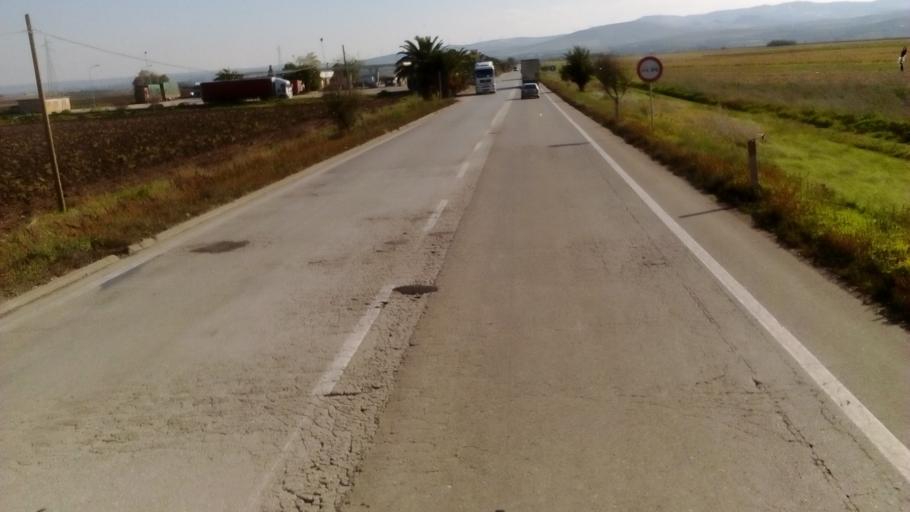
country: IT
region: Apulia
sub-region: Provincia di Foggia
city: Candela
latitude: 41.1112
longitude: 15.5845
